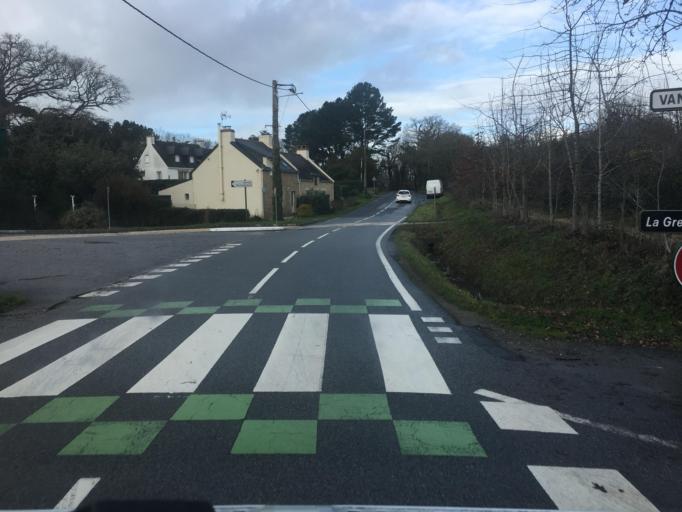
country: FR
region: Brittany
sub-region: Departement du Morbihan
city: Sarzeau
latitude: 47.5166
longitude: -2.7669
